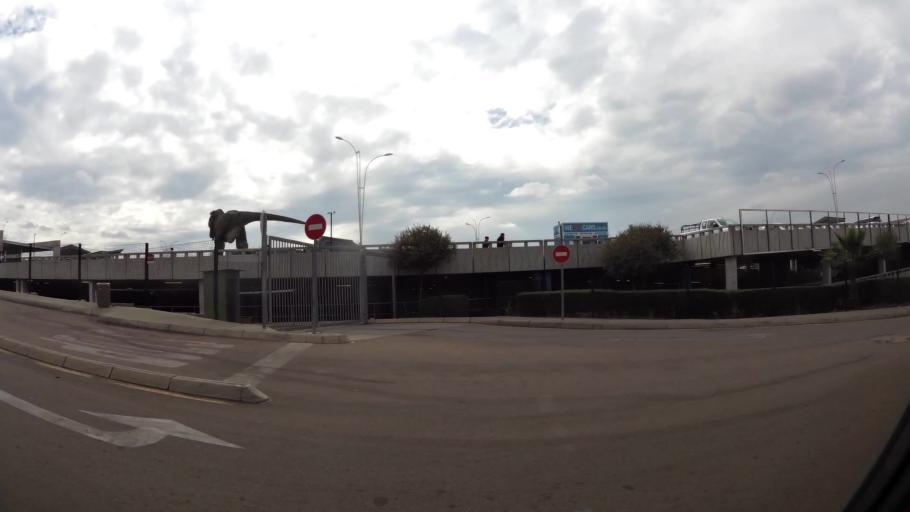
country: ZA
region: Gauteng
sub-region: West Rand District Municipality
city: Muldersdriseloop
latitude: -26.0622
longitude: 27.8368
